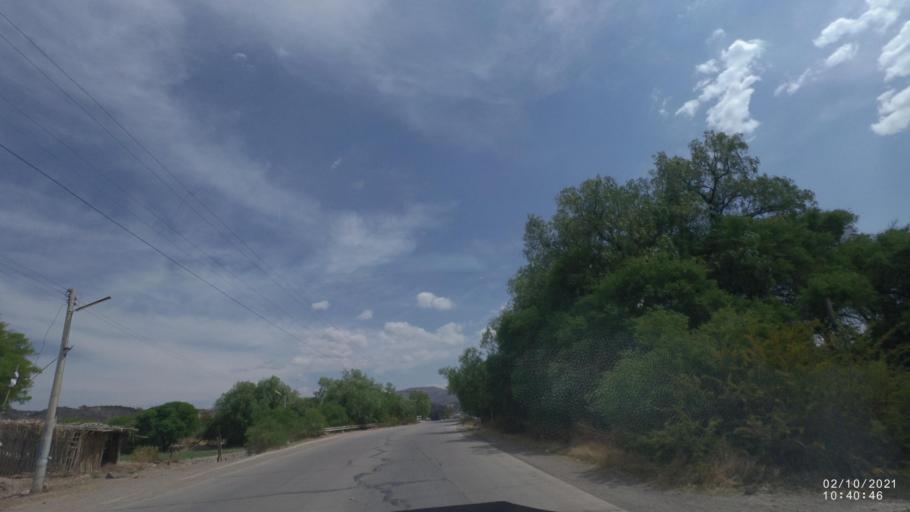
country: BO
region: Cochabamba
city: Capinota
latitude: -17.6186
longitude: -66.2885
